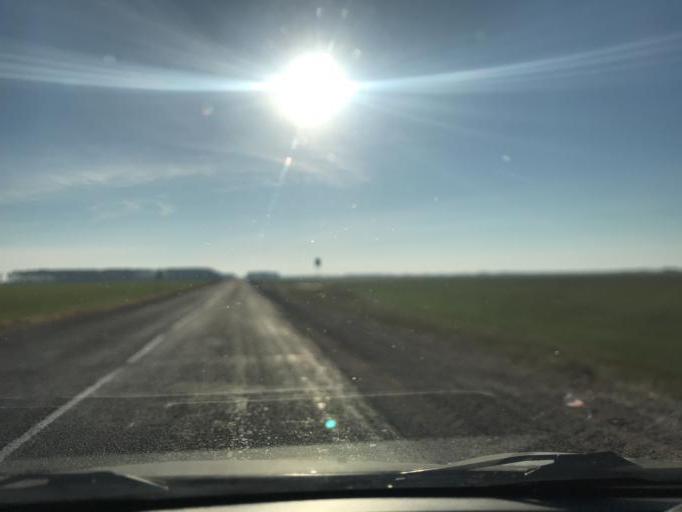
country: BY
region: Gomel
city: Khoyniki
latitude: 51.8244
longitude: 30.0723
